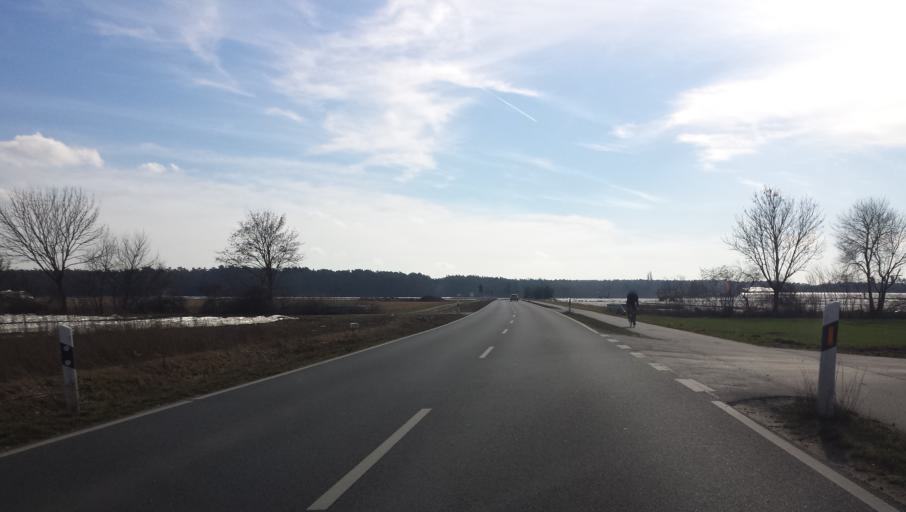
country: DE
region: Hesse
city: Weiterstadt
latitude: 49.9220
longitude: 8.6155
